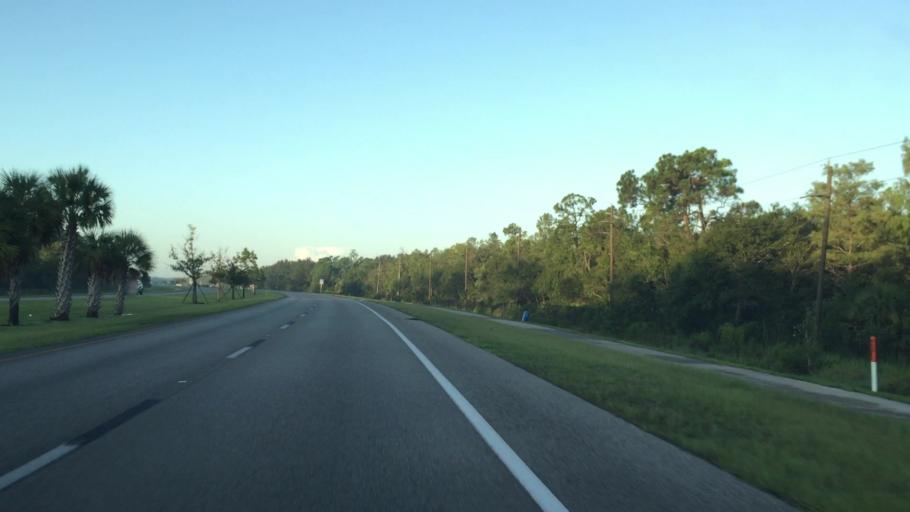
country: US
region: Florida
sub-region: Lee County
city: Fort Myers
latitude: 26.5815
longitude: -81.8231
